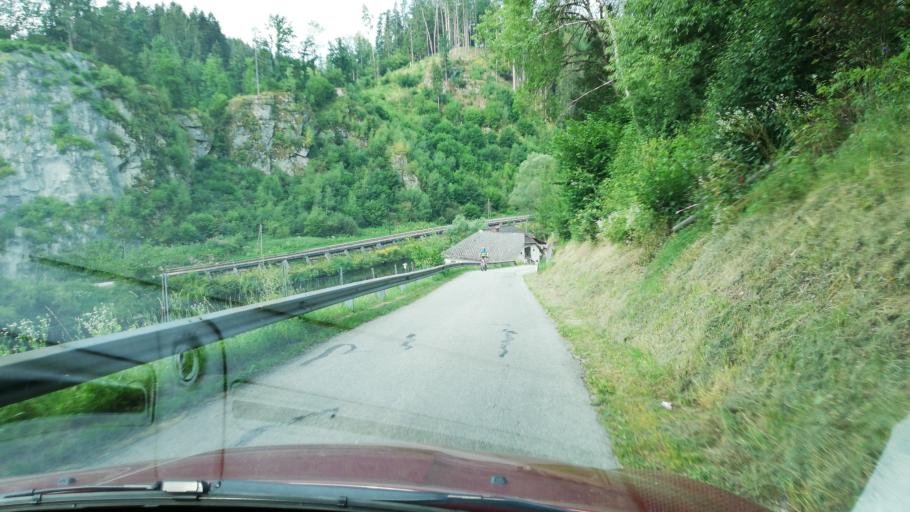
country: AT
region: Upper Austria
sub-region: Politischer Bezirk Rohrbach
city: Kleinzell im Muehlkreis
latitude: 48.5048
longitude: 14.0116
